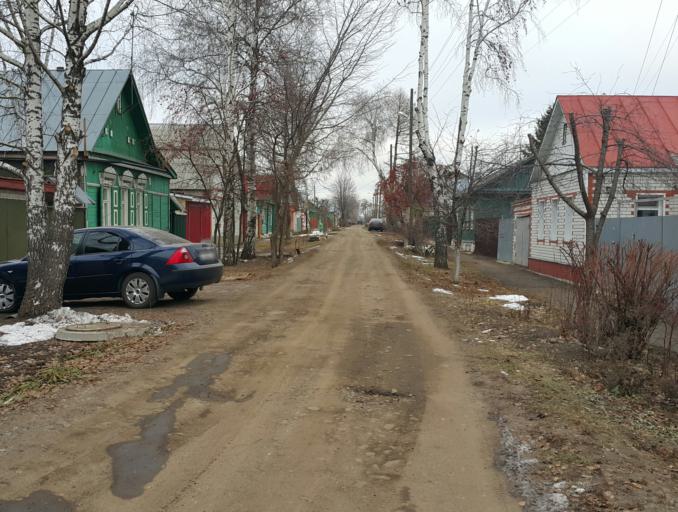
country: RU
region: Tambov
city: Tambov
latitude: 52.7247
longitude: 41.4018
